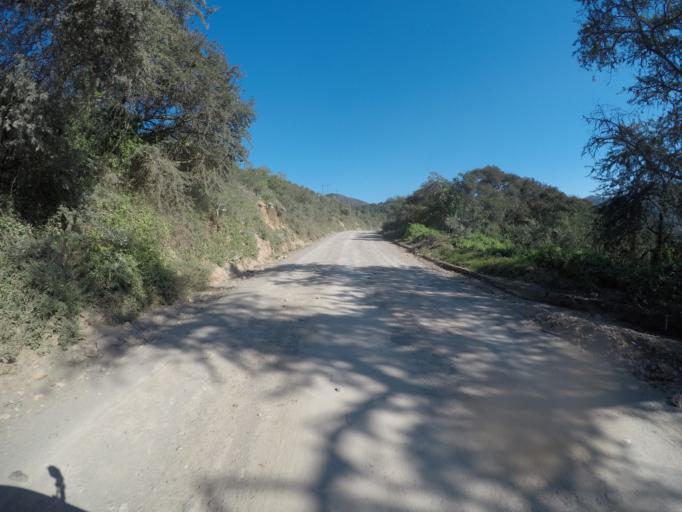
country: ZA
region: Eastern Cape
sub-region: Cacadu District Municipality
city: Kruisfontein
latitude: -33.6710
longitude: 24.5719
